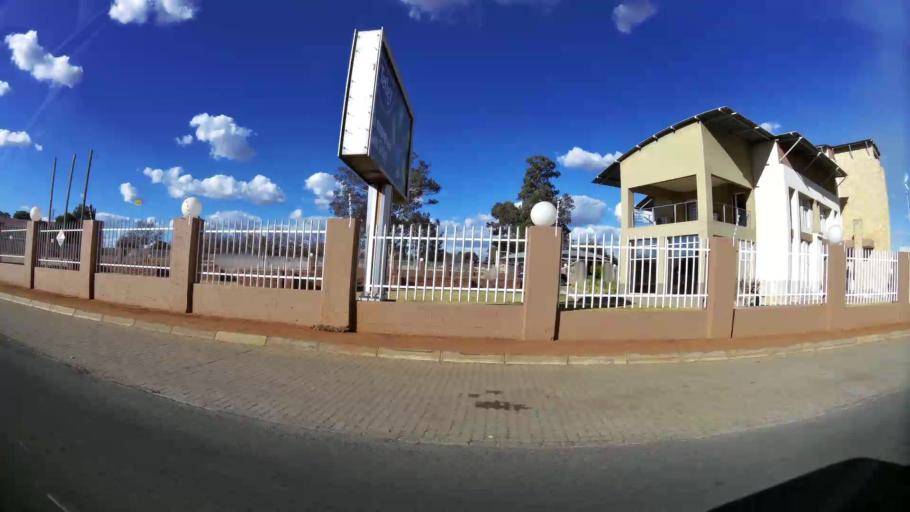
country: ZA
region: North-West
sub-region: Dr Kenneth Kaunda District Municipality
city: Klerksdorp
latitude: -26.8520
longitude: 26.6772
